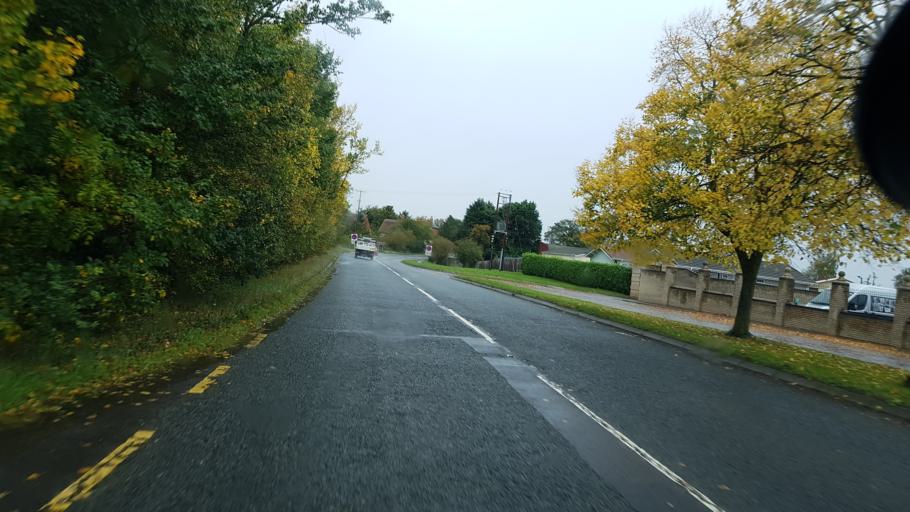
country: GB
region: England
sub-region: Worcestershire
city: Upton upon Severn
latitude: 52.0462
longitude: -2.1731
